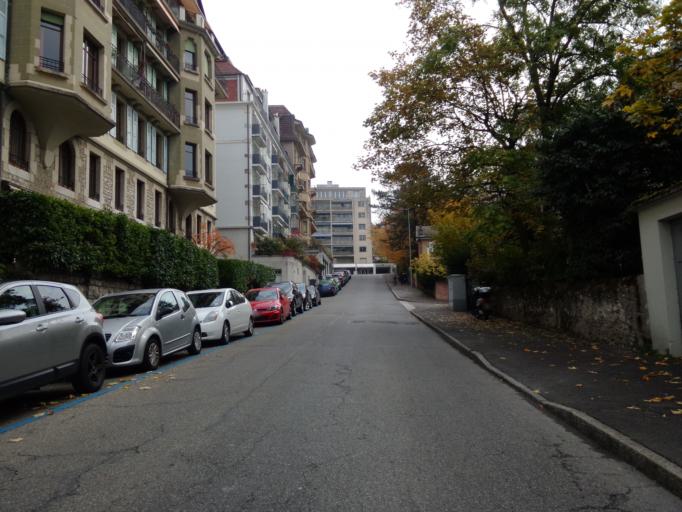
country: CH
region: Geneva
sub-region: Geneva
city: Geneve
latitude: 46.1899
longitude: 6.1508
